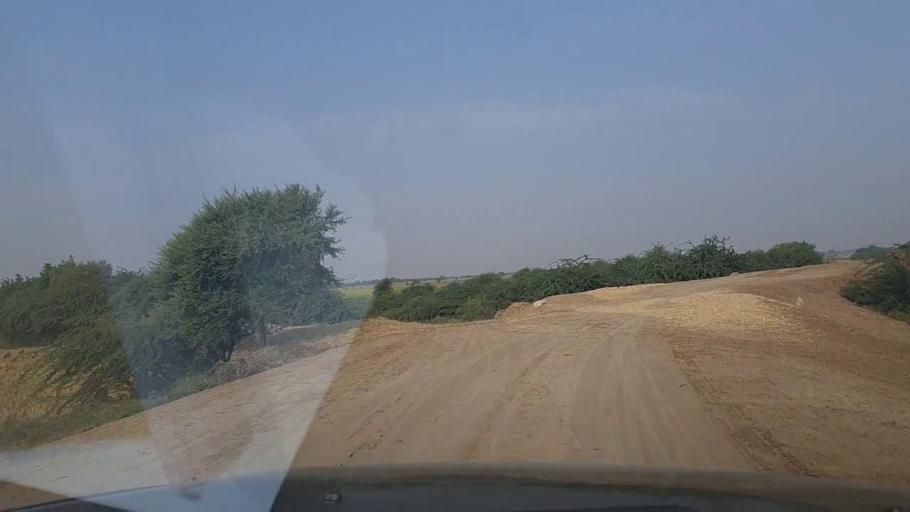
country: PK
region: Sindh
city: Bulri
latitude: 25.0069
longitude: 68.2864
